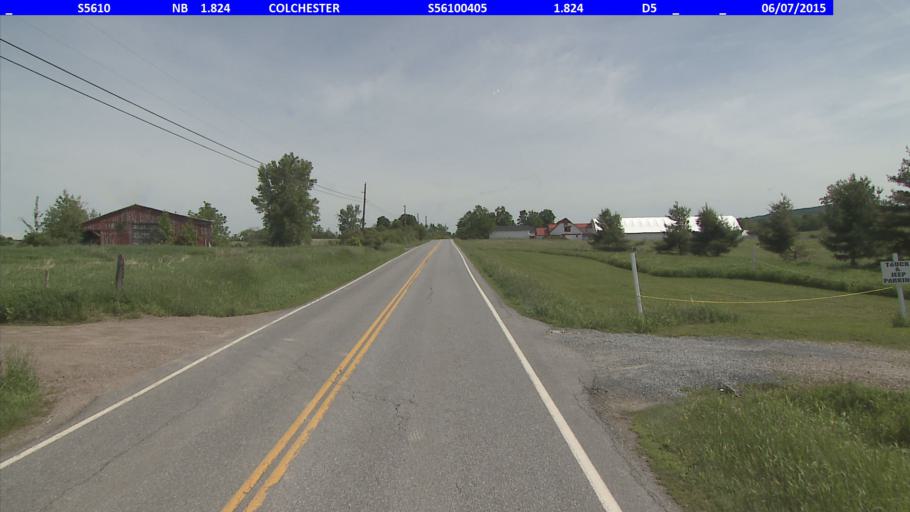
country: US
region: Vermont
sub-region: Chittenden County
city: Colchester
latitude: 44.5660
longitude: -73.1295
